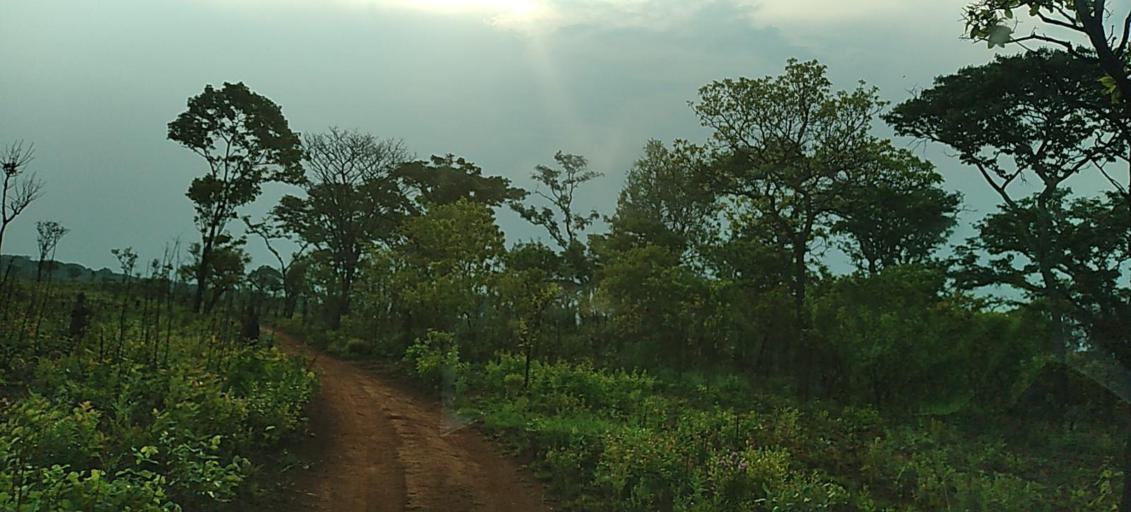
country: ZM
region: North-Western
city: Solwezi
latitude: -12.0423
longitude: 26.0332
